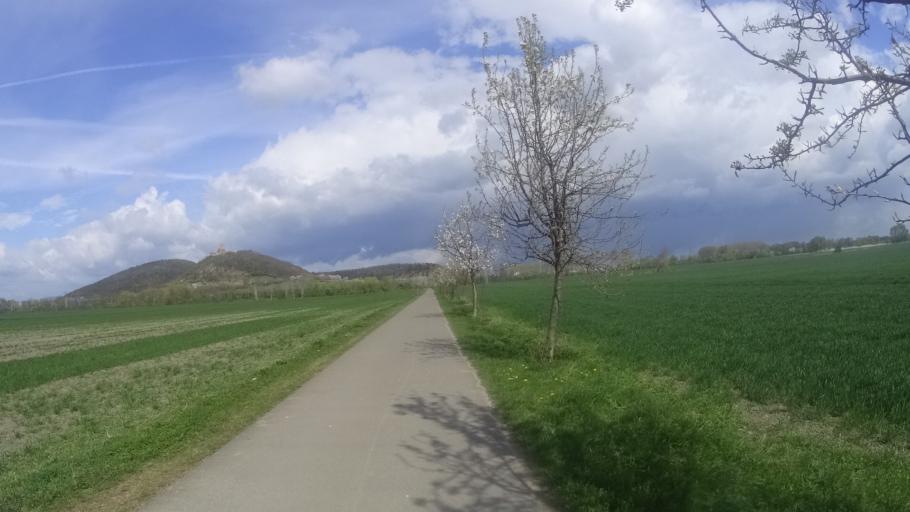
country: DE
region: Thuringia
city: Wandersleben
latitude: 50.8724
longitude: 10.8501
